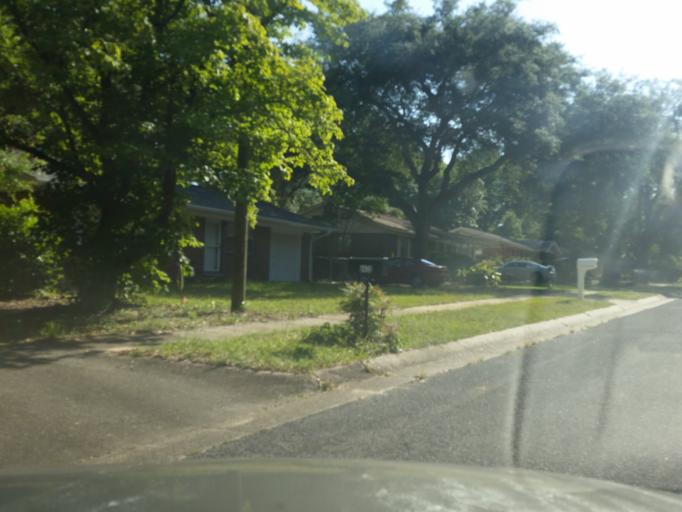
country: US
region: Florida
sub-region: Escambia County
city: Ferry Pass
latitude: 30.5193
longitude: -87.1794
